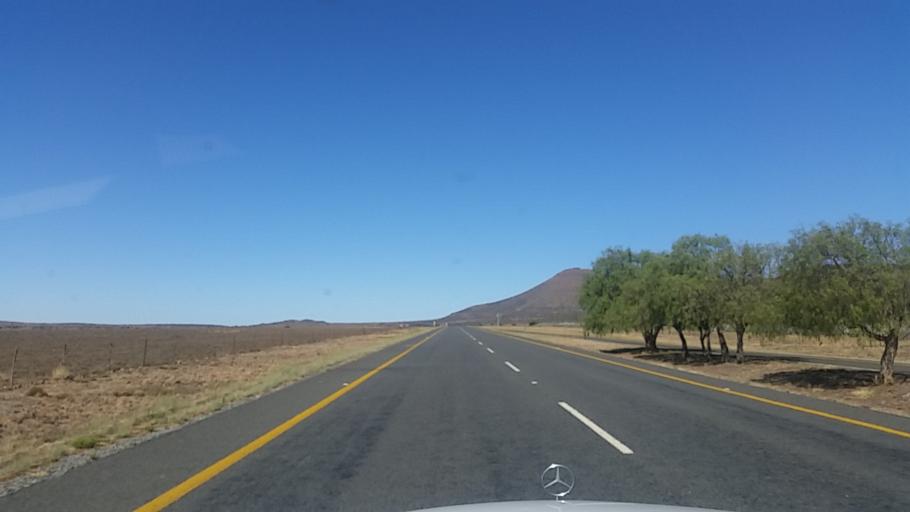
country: ZA
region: Eastern Cape
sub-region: Cacadu District Municipality
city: Graaff-Reinet
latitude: -32.0234
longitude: 24.6351
